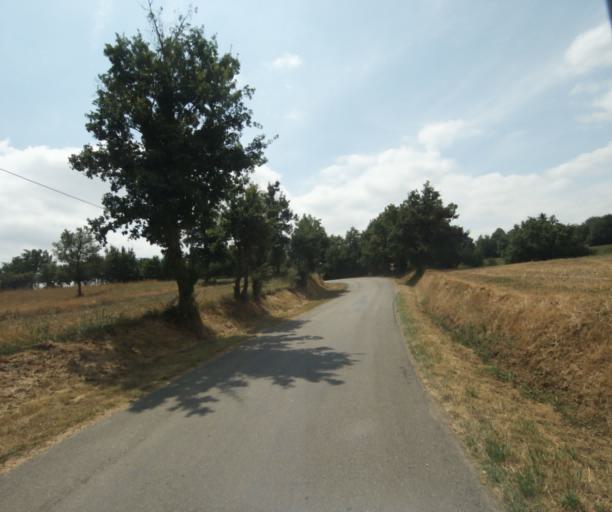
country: FR
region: Midi-Pyrenees
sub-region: Departement de la Haute-Garonne
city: Revel
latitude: 43.4418
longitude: 1.9725
